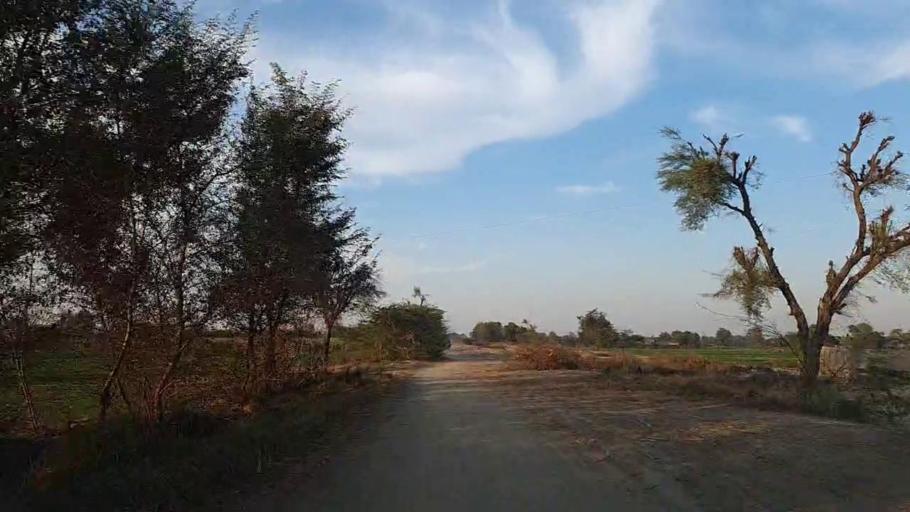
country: PK
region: Sindh
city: Bandhi
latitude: 26.6002
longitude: 68.3590
